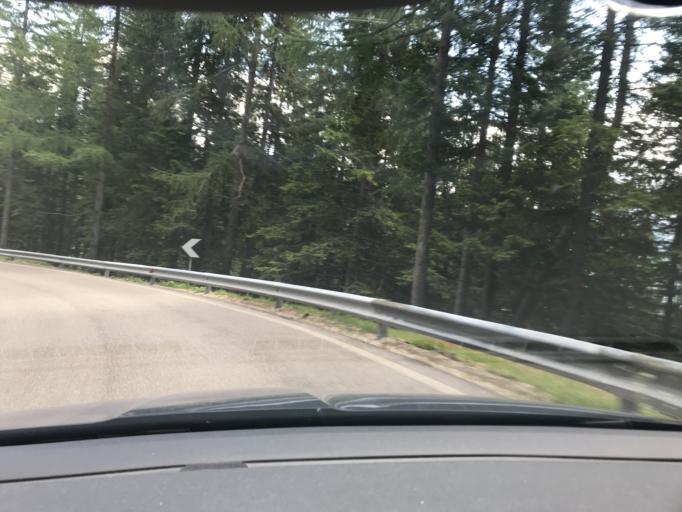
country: IT
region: Veneto
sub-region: Provincia di Belluno
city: Cortina d'Ampezzo
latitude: 46.5201
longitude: 12.0956
